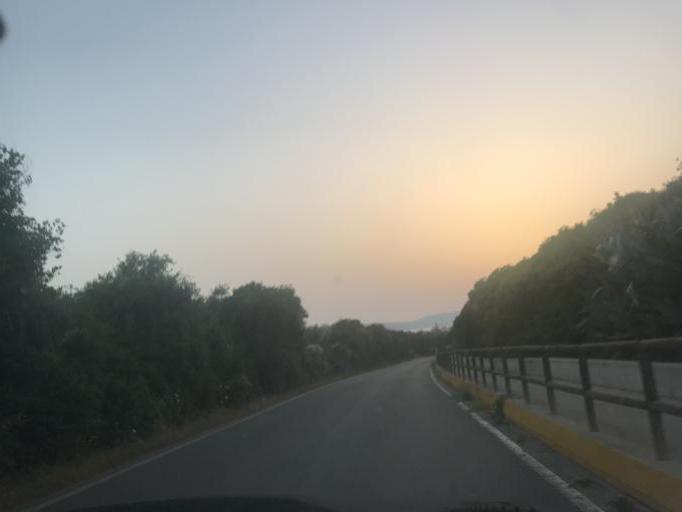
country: IT
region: Sardinia
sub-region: Provincia di Sassari
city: Alghero
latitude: 40.5539
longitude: 8.3346
